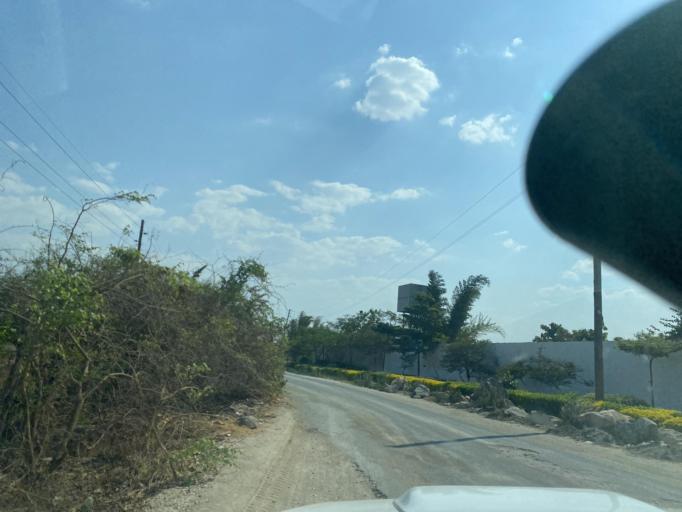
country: ZM
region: Lusaka
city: Lusaka
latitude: -15.3581
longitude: 28.1021
